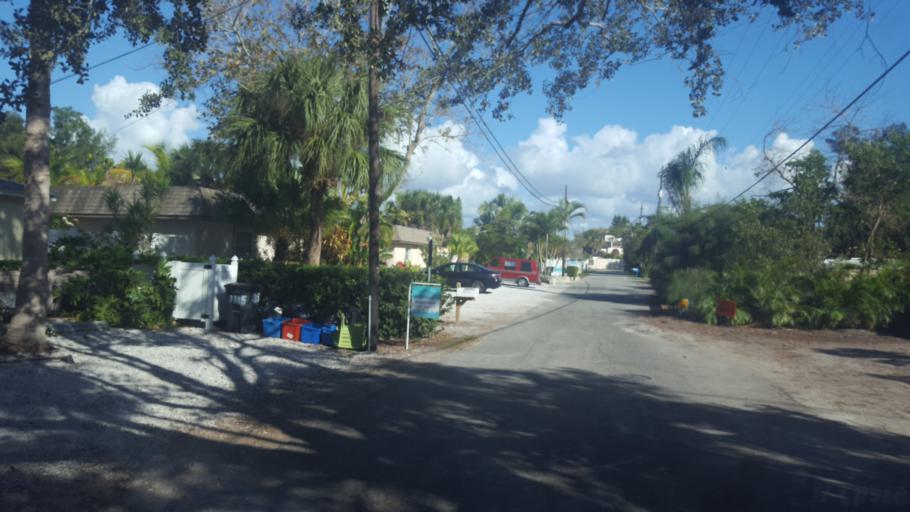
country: US
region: Florida
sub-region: Sarasota County
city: Gulf Gate Estates
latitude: 27.2463
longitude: -82.5323
